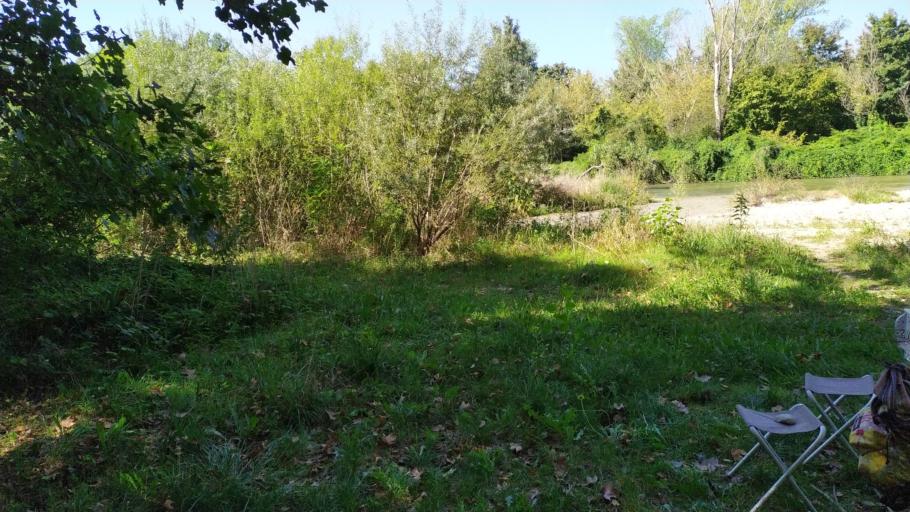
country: IT
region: Friuli Venezia Giulia
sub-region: Provincia di Pordenone
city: Cavolano-Schiavoi
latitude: 45.9386
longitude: 12.4876
